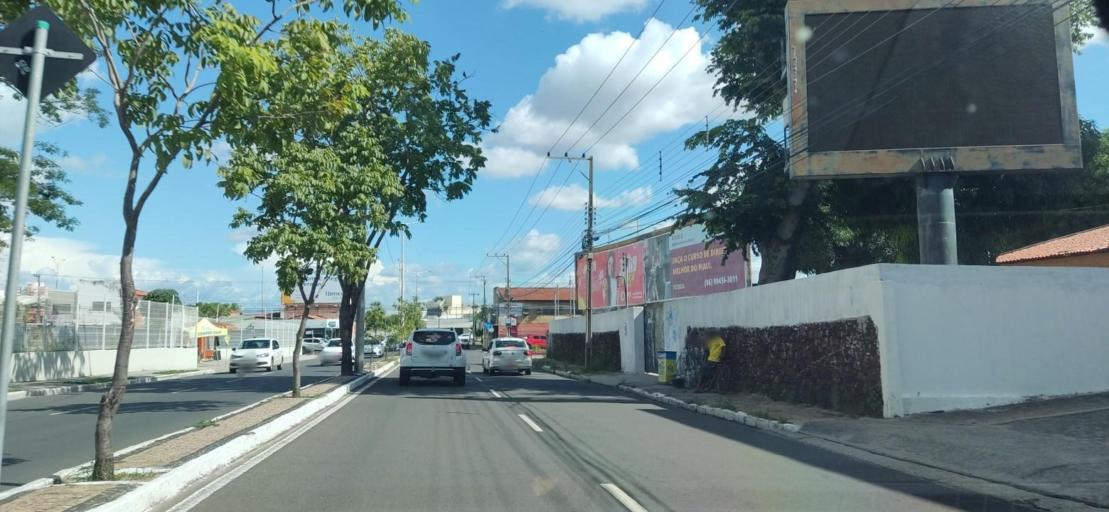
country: BR
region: Piaui
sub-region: Teresina
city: Teresina
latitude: -5.0788
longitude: -42.7901
